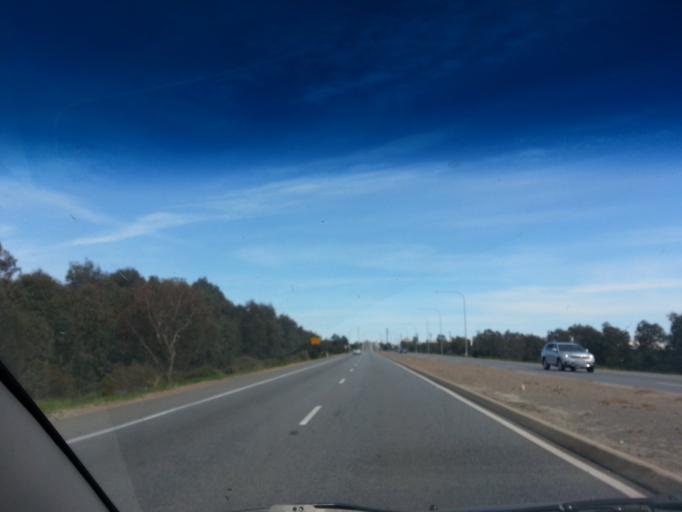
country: AU
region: South Australia
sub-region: Port Adelaide Enfield
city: Alberton
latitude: -34.8357
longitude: 138.5283
